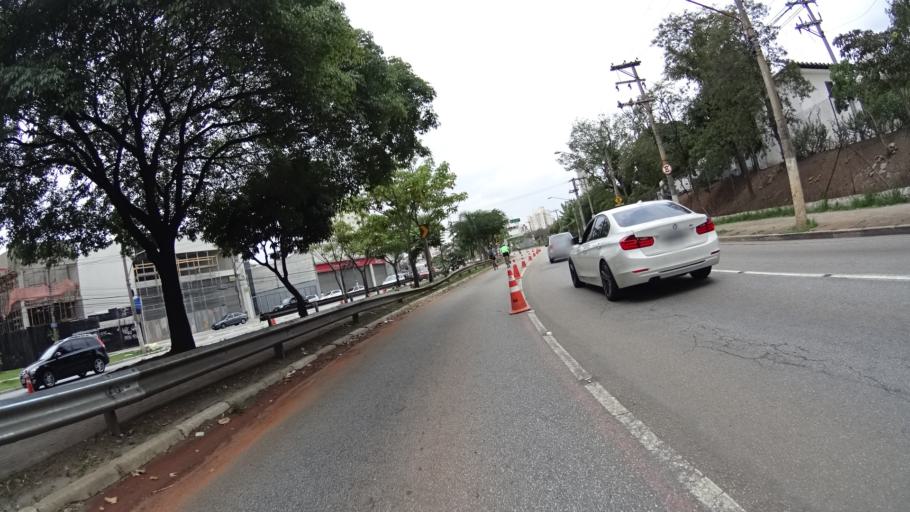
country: BR
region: Sao Paulo
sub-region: Sao Paulo
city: Sao Paulo
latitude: -23.5028
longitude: -46.6193
